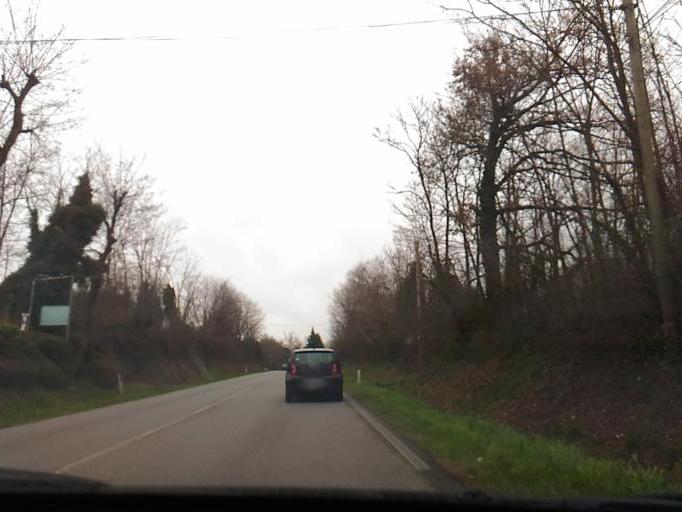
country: IT
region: Lombardy
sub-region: Provincia di Como
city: Figino Serenza
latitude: 45.7012
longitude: 9.1521
